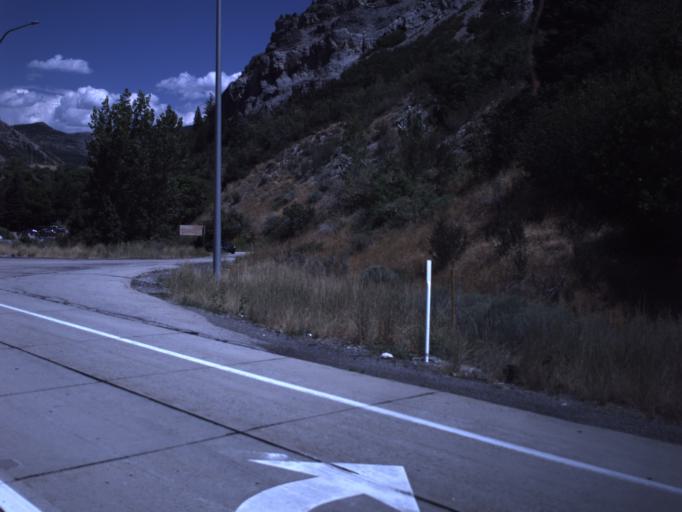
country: US
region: Utah
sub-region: Utah County
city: Orem
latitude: 40.3365
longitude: -111.6111
